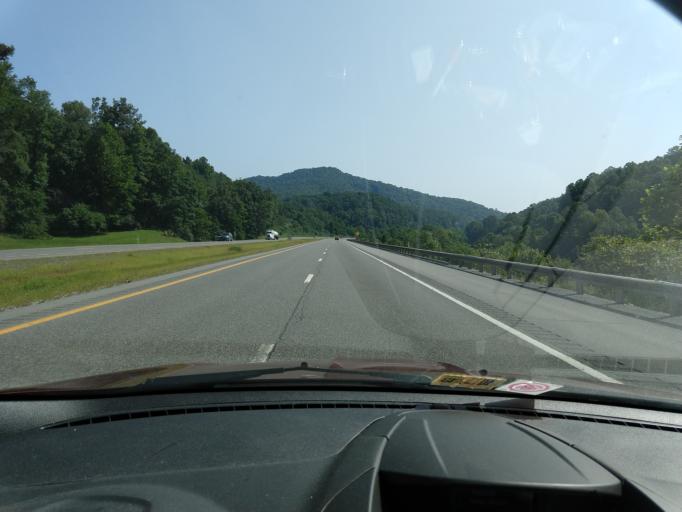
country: US
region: West Virginia
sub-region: Braxton County
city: Sutton
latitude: 38.6879
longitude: -80.6945
